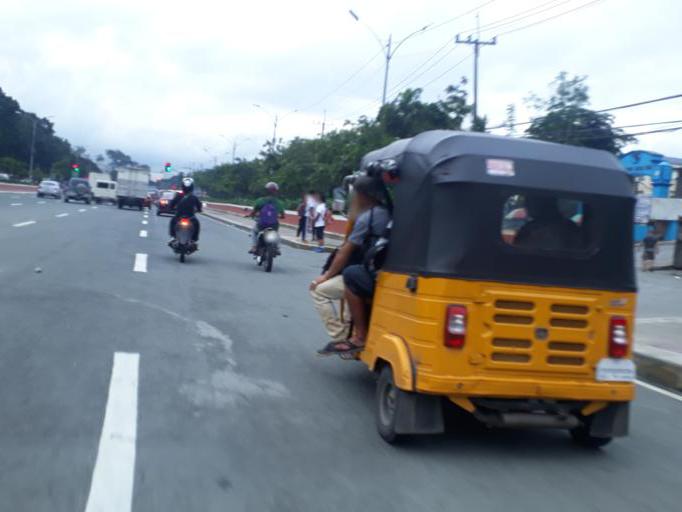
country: PH
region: Calabarzon
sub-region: Province of Rizal
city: San Mateo
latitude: 14.6899
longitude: 121.0947
